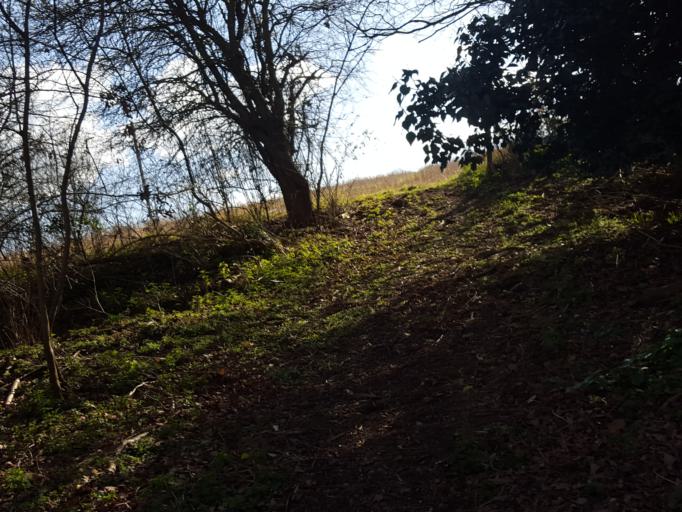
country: GB
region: England
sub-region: Essex
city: Little Clacton
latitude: 51.8680
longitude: 1.1150
